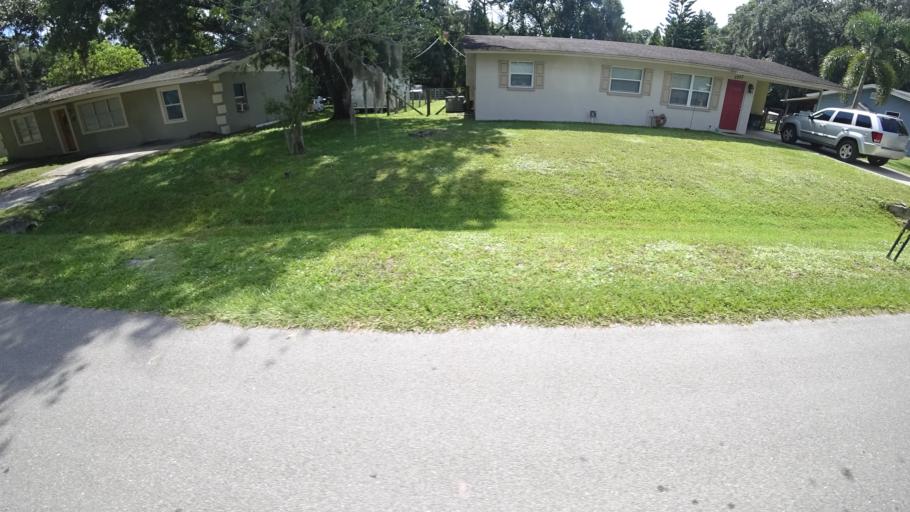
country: US
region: Florida
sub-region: Manatee County
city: Samoset
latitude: 27.4739
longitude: -82.4858
